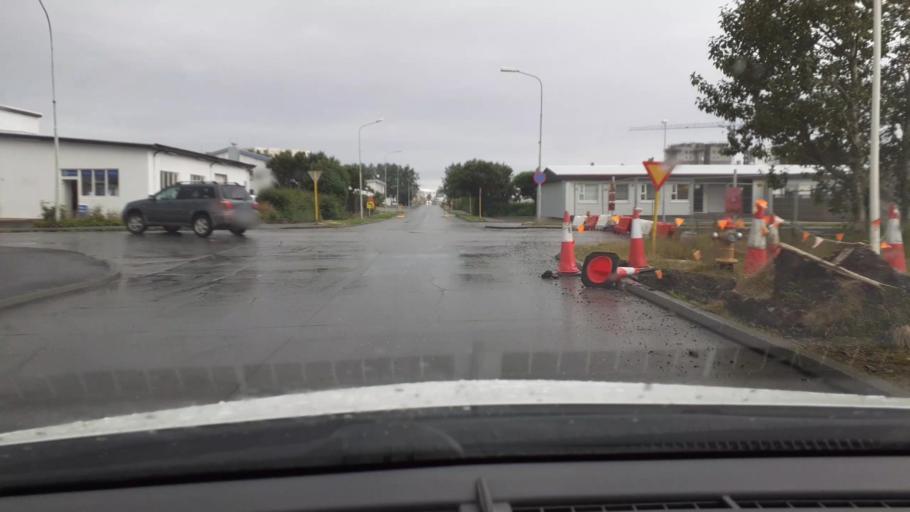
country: IS
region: West
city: Akranes
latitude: 64.3234
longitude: -22.0646
